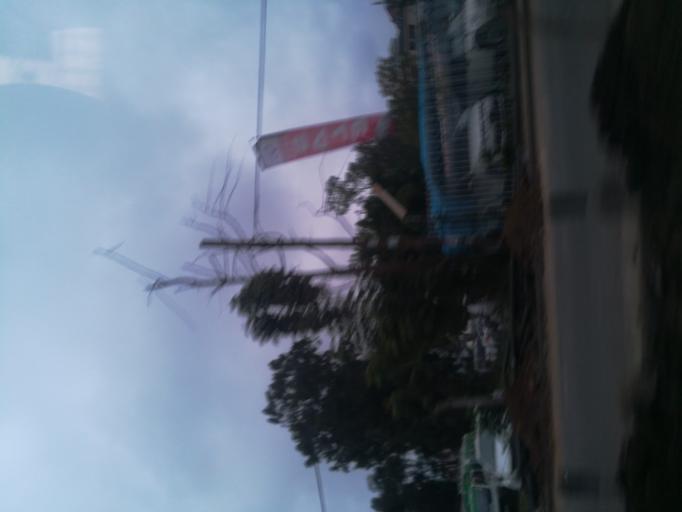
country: KE
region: Nairobi Area
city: Nairobi
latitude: -1.2924
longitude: 36.7886
